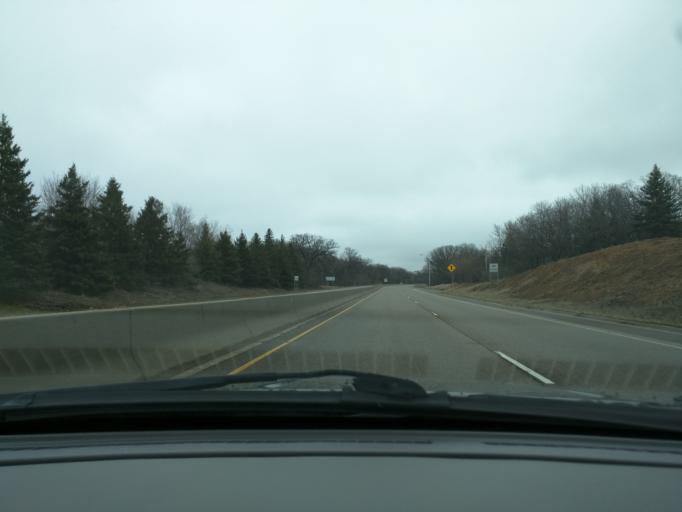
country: US
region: Minnesota
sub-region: Hennepin County
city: Minnetonka
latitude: 44.9172
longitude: -93.4933
